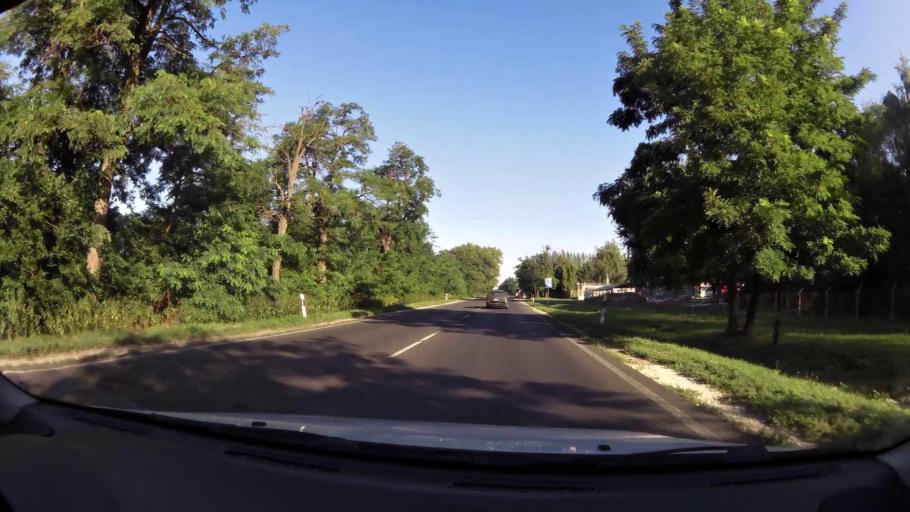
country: HU
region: Pest
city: Pilis
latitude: 47.3001
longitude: 19.5185
